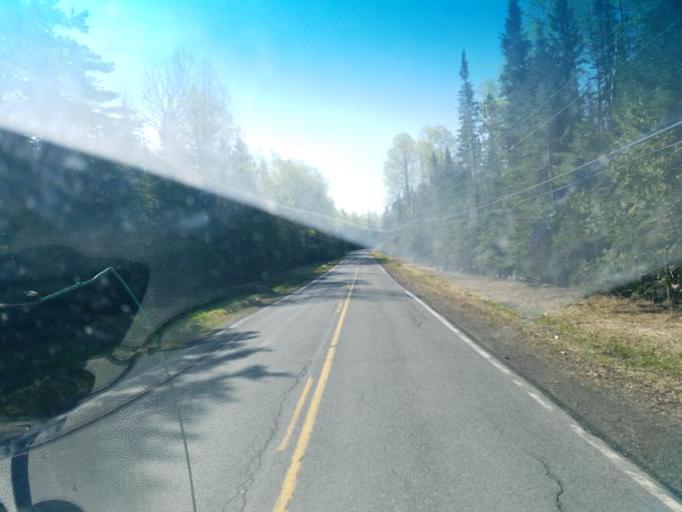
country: US
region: Maine
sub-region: Aroostook County
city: Caribou
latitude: 46.8514
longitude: -68.1990
